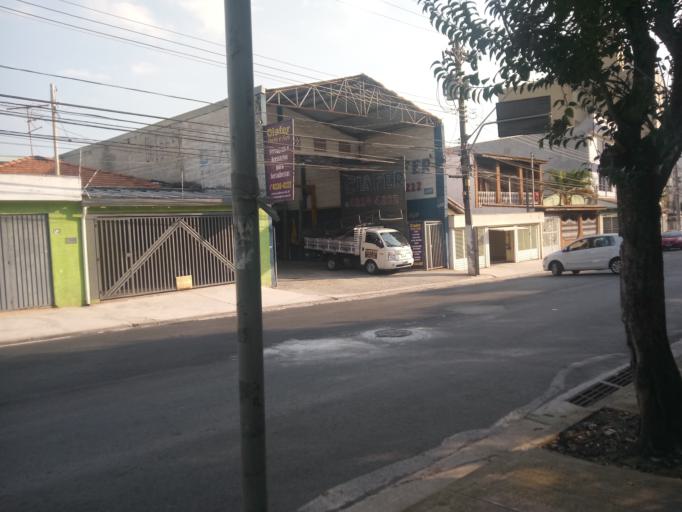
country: BR
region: Sao Paulo
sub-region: Sao Bernardo Do Campo
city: Sao Bernardo do Campo
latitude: -23.6995
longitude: -46.5460
